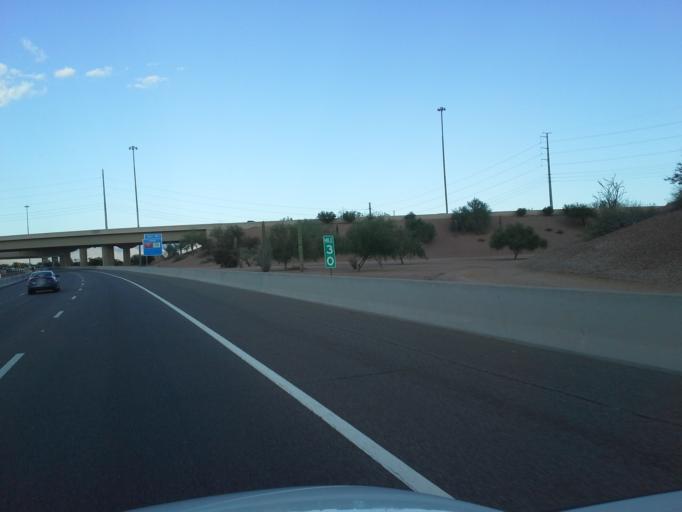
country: US
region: Arizona
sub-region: Maricopa County
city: Paradise Valley
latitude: 33.6716
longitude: -112.0007
